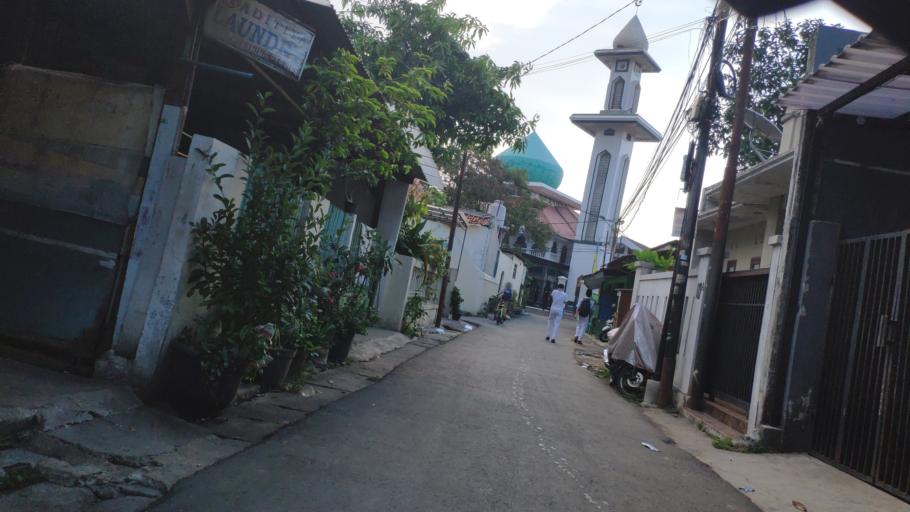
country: ID
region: West Java
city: Pamulang
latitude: -6.2897
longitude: 106.8039
